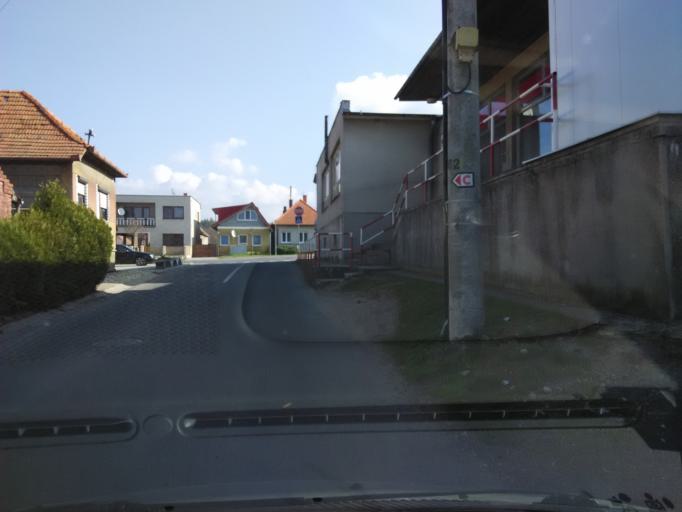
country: SK
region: Nitriansky
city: Zlate Moravce
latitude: 48.4115
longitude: 18.4321
